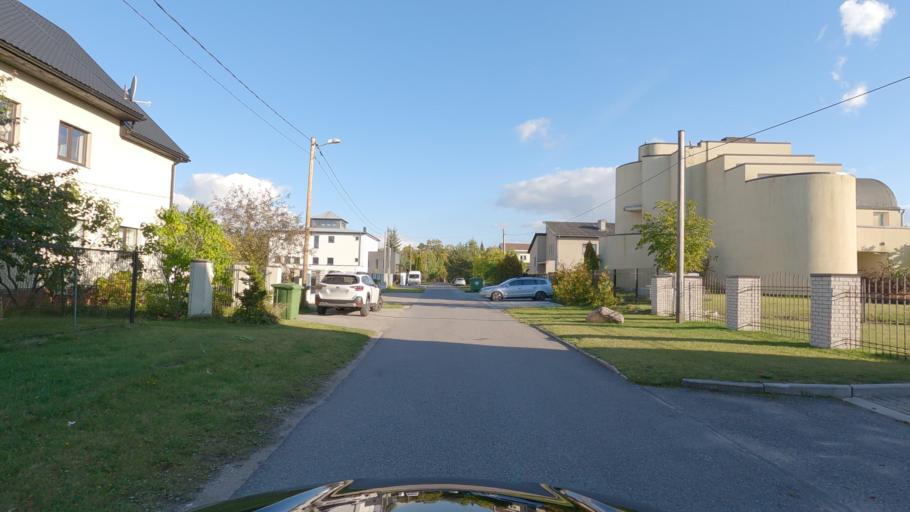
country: EE
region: Harju
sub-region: Saue vald
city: Laagri
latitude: 59.3510
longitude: 24.6416
